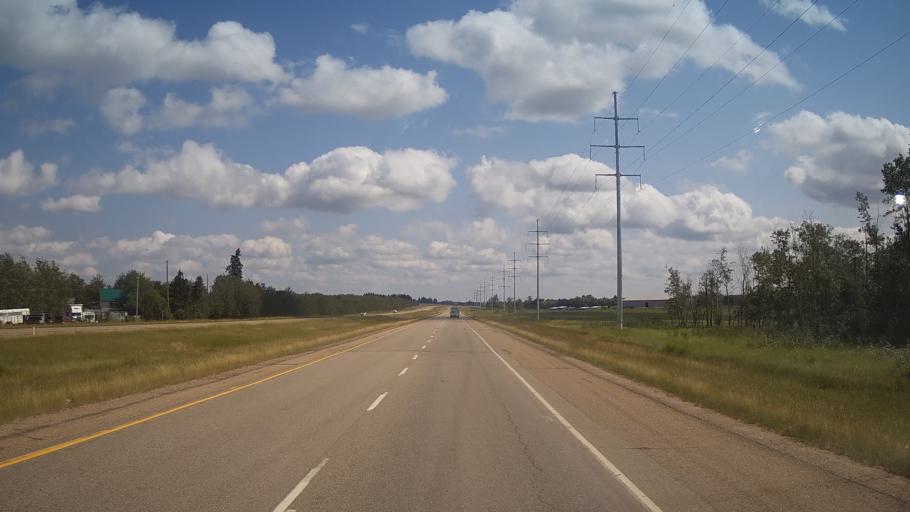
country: CA
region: Alberta
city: Sherwood Park
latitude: 53.4413
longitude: -113.2192
